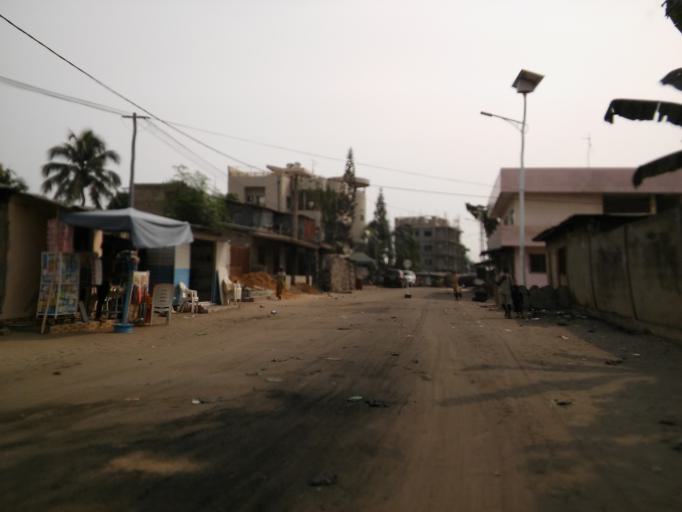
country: BJ
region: Littoral
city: Cotonou
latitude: 6.3930
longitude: 2.3799
